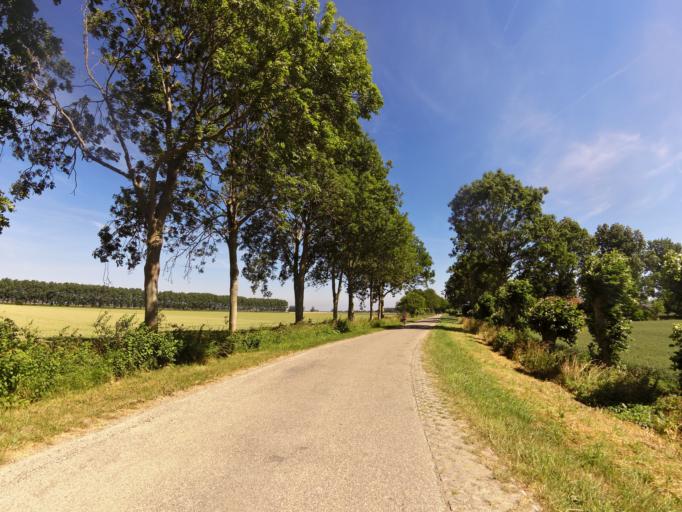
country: NL
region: Zeeland
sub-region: Gemeente Sluis
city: Sluis
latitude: 51.3226
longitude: 3.3721
